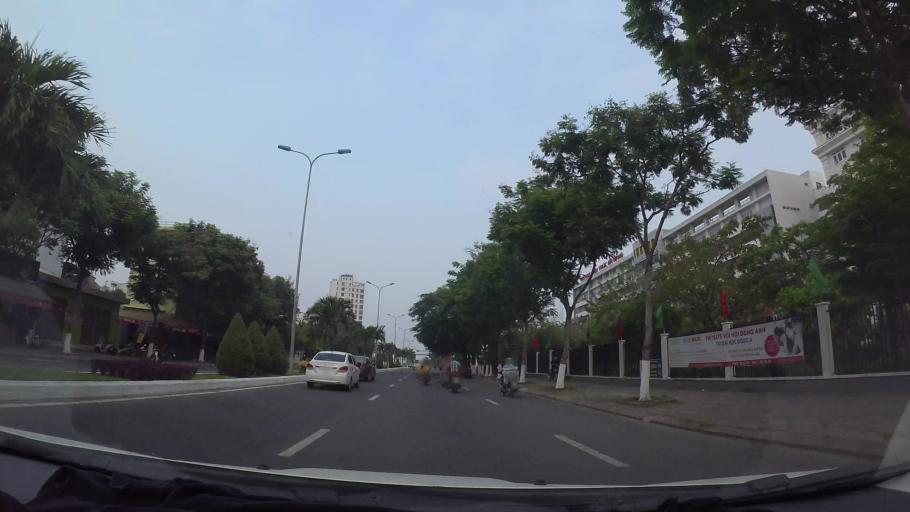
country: VN
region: Da Nang
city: Cam Le
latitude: 16.0326
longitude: 108.2214
